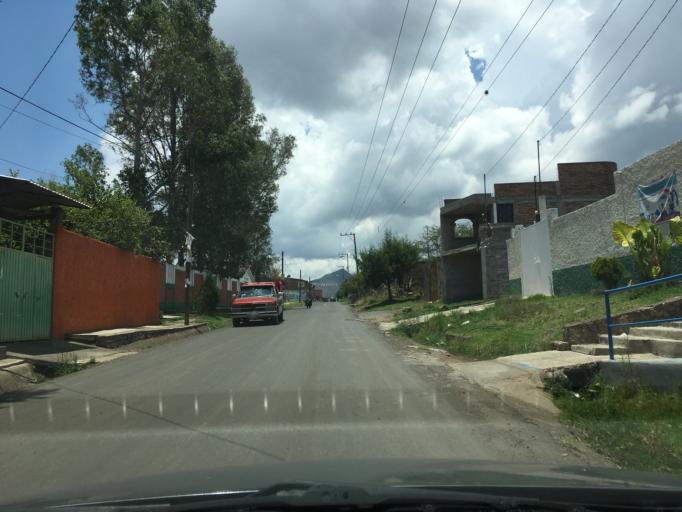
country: MX
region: Michoacan
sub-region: Morelia
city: La Mintzita (Piedra Dura)
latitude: 19.5949
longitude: -101.2792
